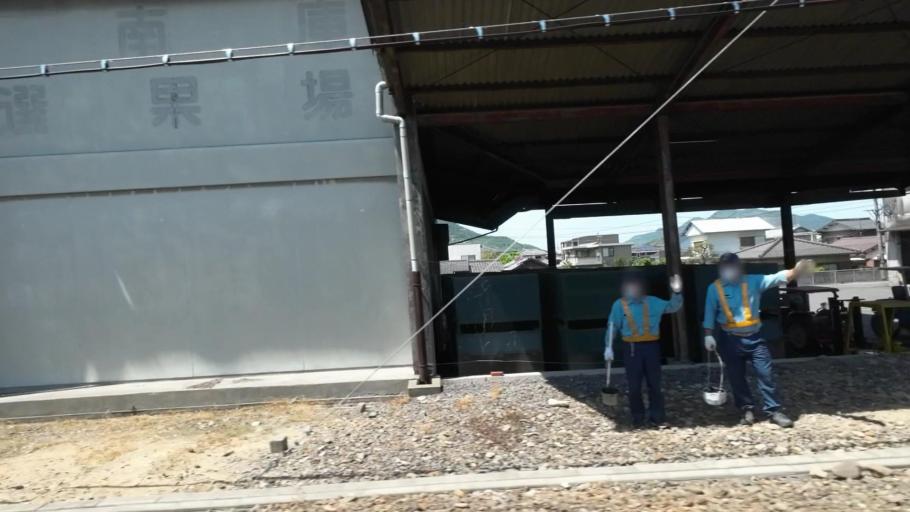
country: JP
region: Kagawa
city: Marugame
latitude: 34.2333
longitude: 133.7874
